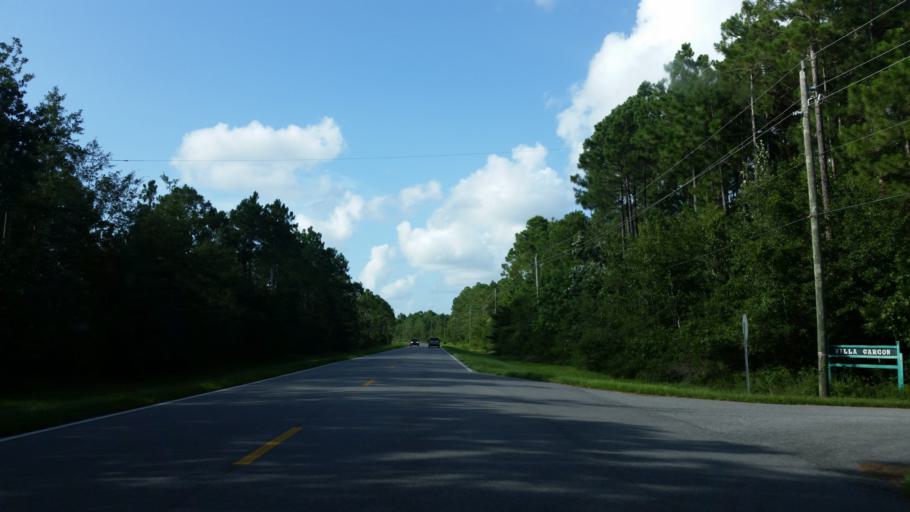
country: US
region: Florida
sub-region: Santa Rosa County
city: Bagdad
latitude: 30.5158
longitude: -87.0547
